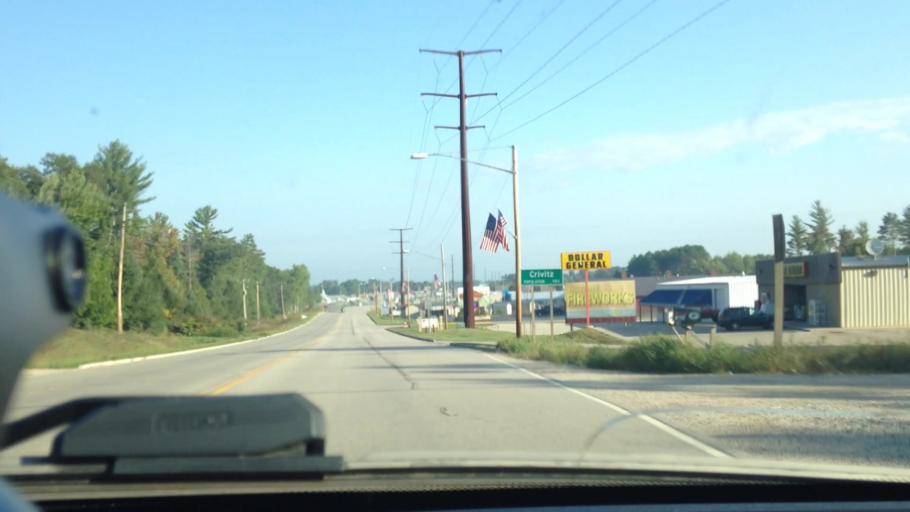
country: US
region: Wisconsin
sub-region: Marinette County
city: Peshtigo
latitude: 45.2163
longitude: -87.9964
